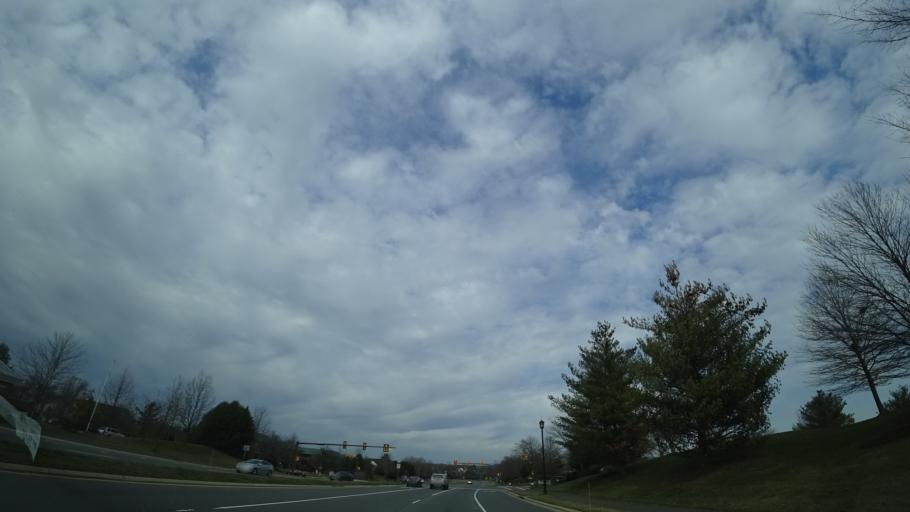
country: US
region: Virginia
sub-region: Loudoun County
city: Ashburn
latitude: 39.0354
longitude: -77.5046
